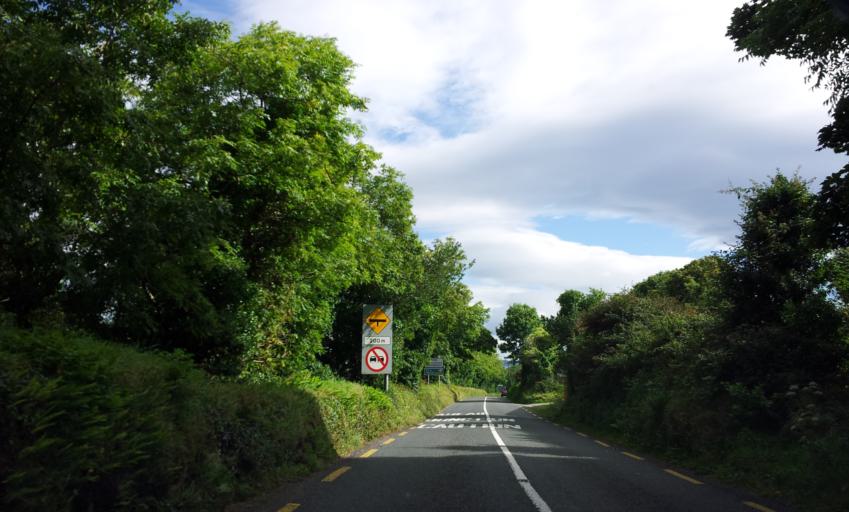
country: IE
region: Munster
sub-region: Ciarrai
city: Killorglin
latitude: 52.2241
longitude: -9.9016
